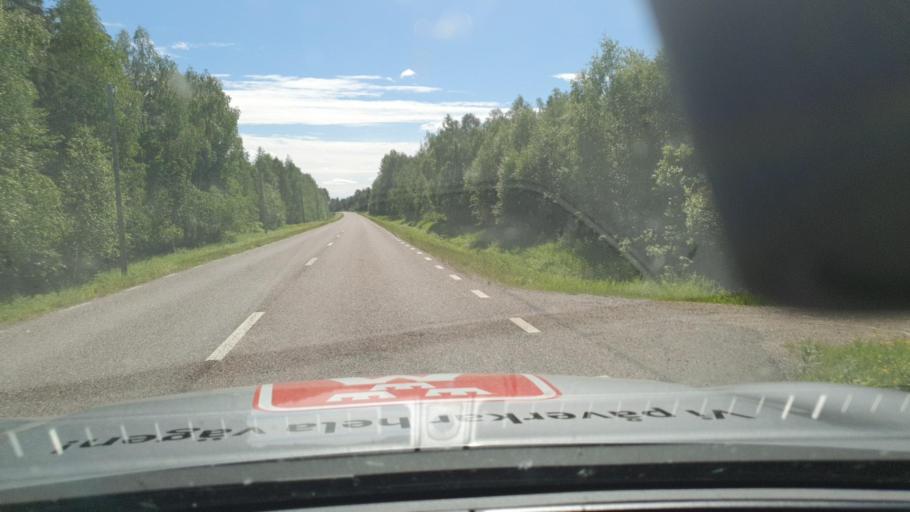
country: FI
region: Lapland
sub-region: Torniolaakso
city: Pello
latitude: 66.9368
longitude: 23.8509
